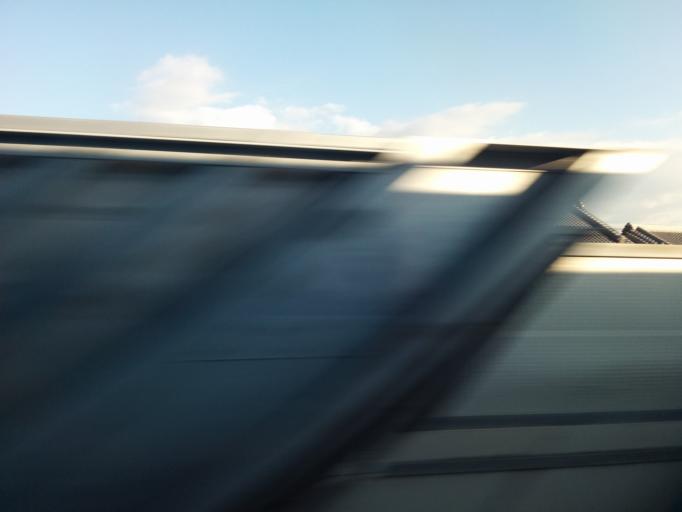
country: JP
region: Aichi
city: Gamagori
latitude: 34.8150
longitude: 137.2841
